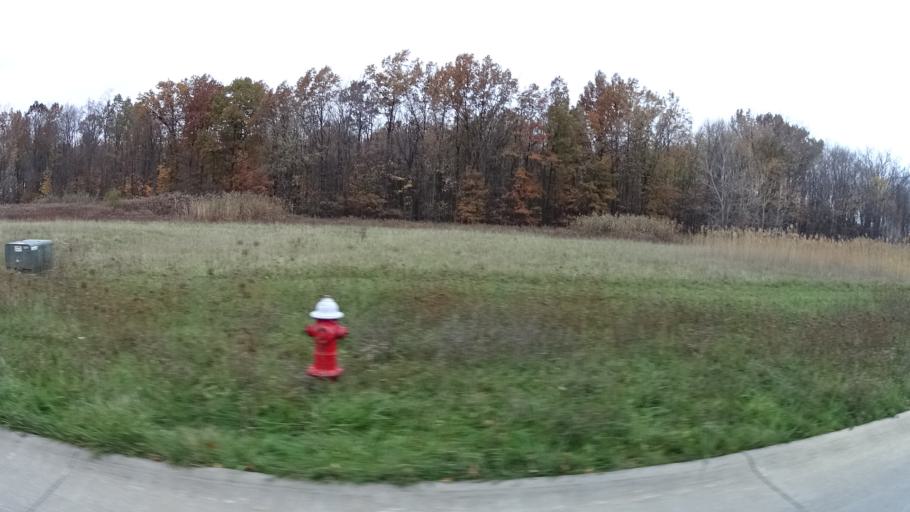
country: US
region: Ohio
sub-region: Lorain County
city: Amherst
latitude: 41.4354
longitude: -82.2217
